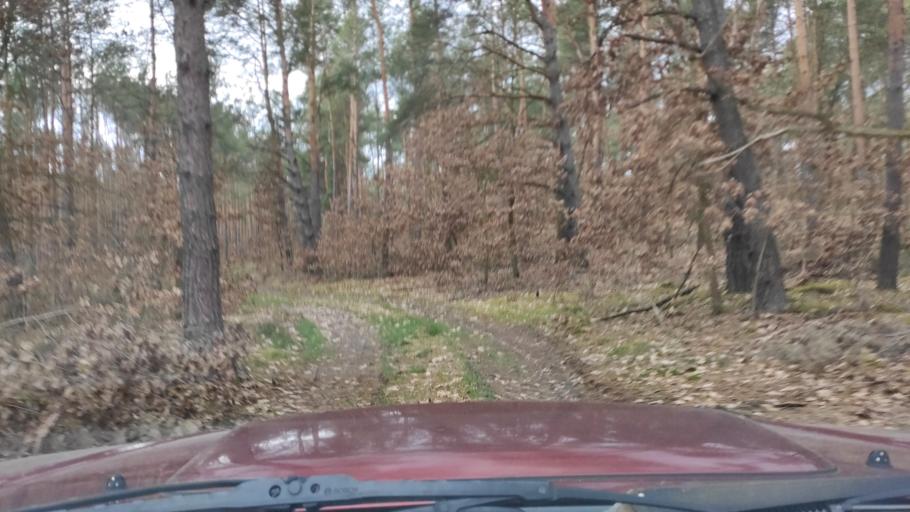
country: PL
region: Masovian Voivodeship
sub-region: Powiat kozienicki
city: Garbatka-Letnisko
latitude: 51.5140
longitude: 21.5678
